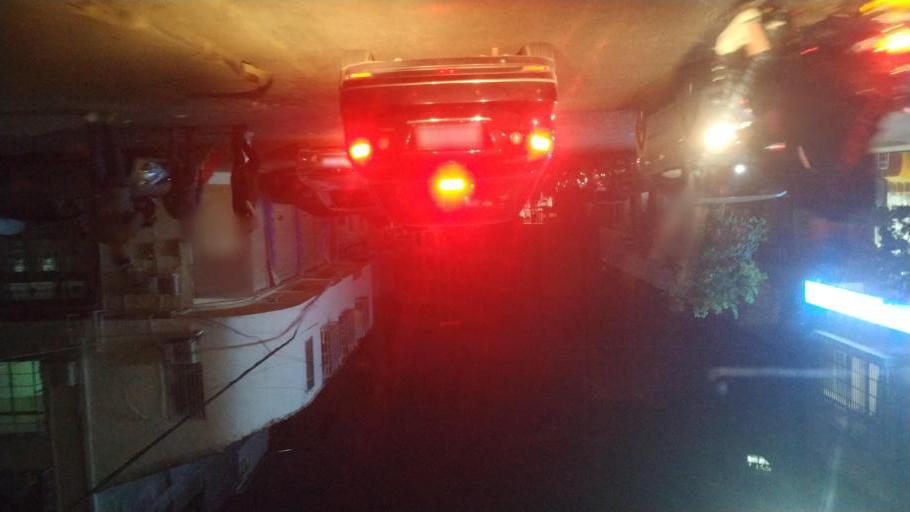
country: CN
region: Guangdong
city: Xiaguo
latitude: 21.6471
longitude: 110.6310
